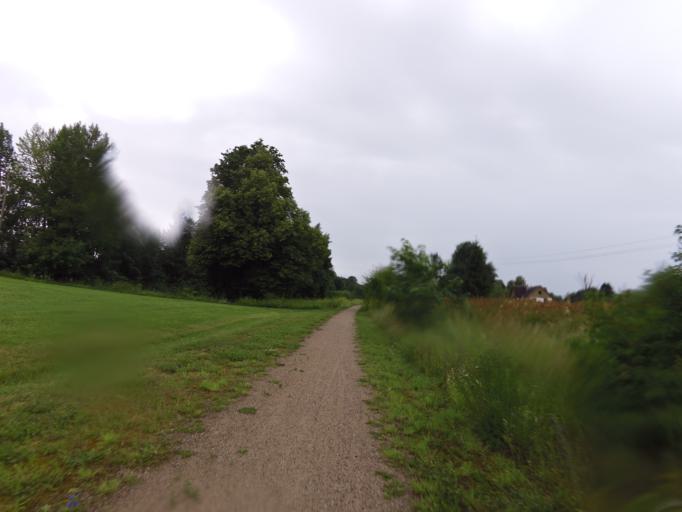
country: EE
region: Harju
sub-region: Nissi vald
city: Turba
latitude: 58.9986
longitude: 24.0562
